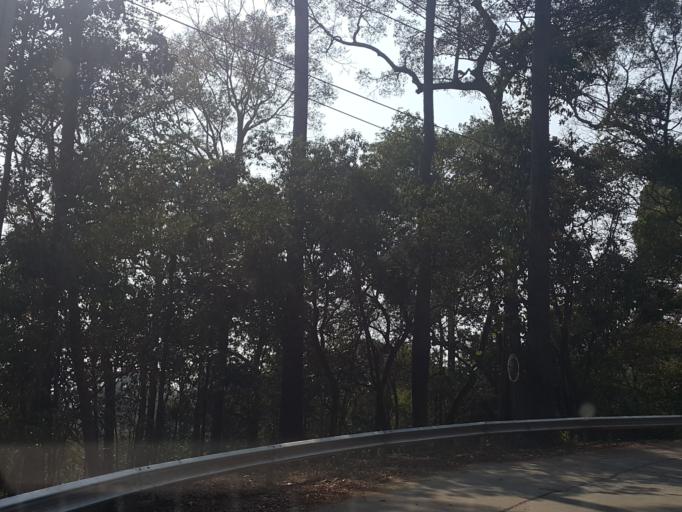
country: TH
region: Chiang Mai
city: Mae Taeng
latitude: 19.0209
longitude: 98.7982
